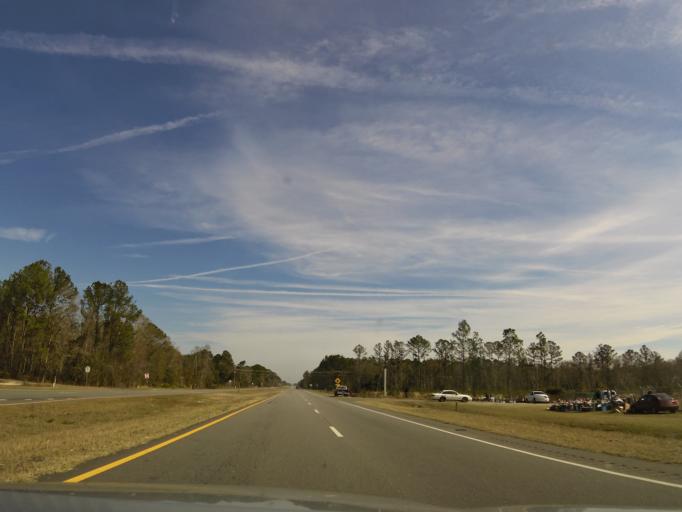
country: US
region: Georgia
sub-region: Brantley County
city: Nahunta
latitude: 31.2140
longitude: -81.9051
